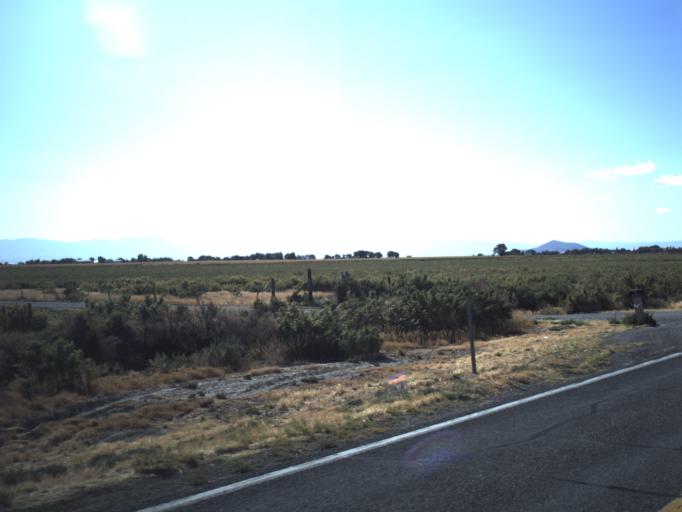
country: US
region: Utah
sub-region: Millard County
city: Delta
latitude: 39.3092
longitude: -112.6525
